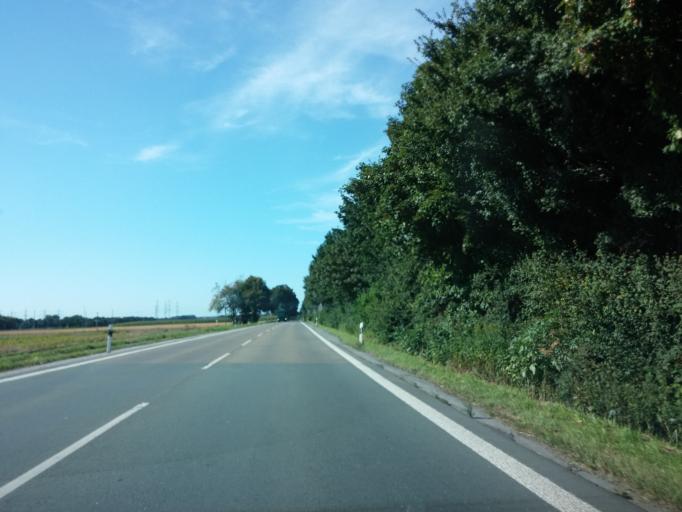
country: DE
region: North Rhine-Westphalia
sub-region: Regierungsbezirk Munster
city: Gladbeck
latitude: 51.6141
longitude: 7.0216
